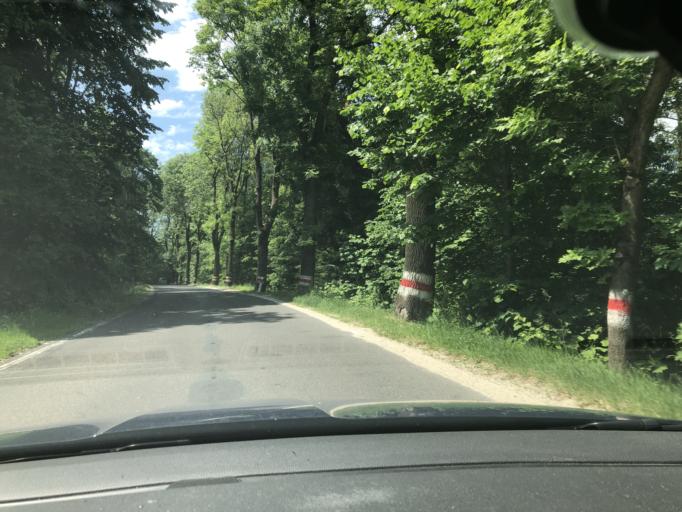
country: PL
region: Lower Silesian Voivodeship
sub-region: Powiat zlotoryjski
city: Swierzawa
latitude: 50.9644
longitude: 15.8365
